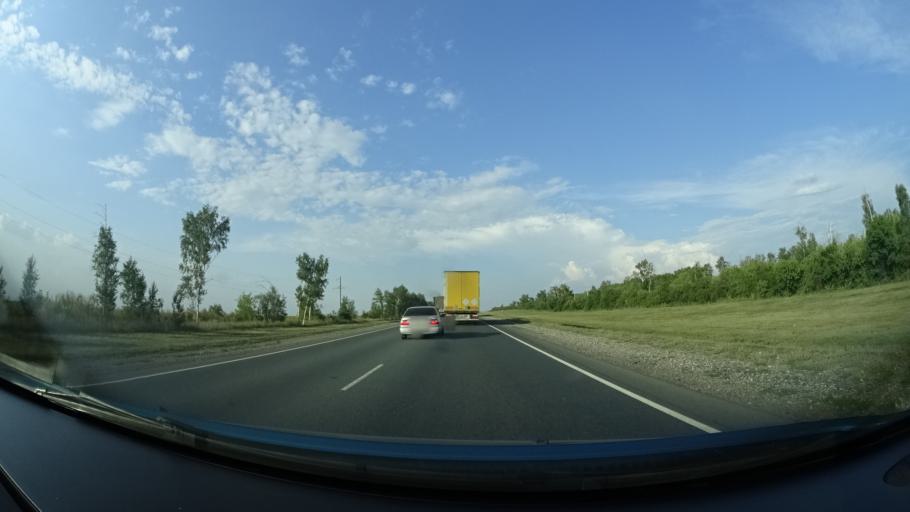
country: RU
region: Samara
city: Krasnyy Yar
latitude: 53.6678
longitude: 50.7628
